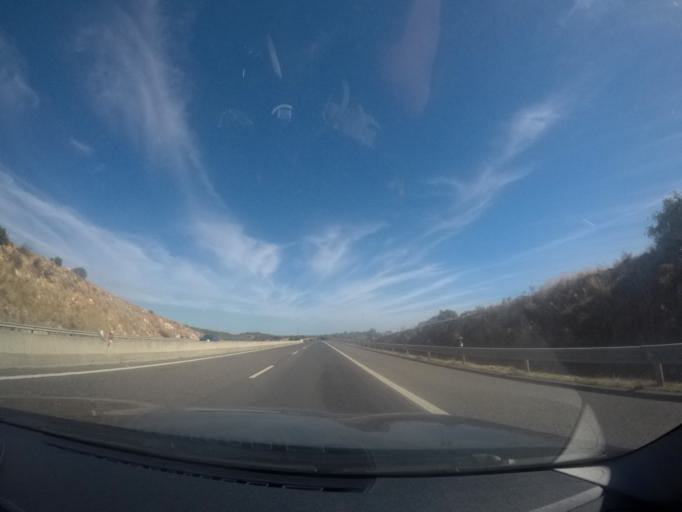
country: PT
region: Faro
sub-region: Lagoa
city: Estombar
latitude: 37.1676
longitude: -8.5136
